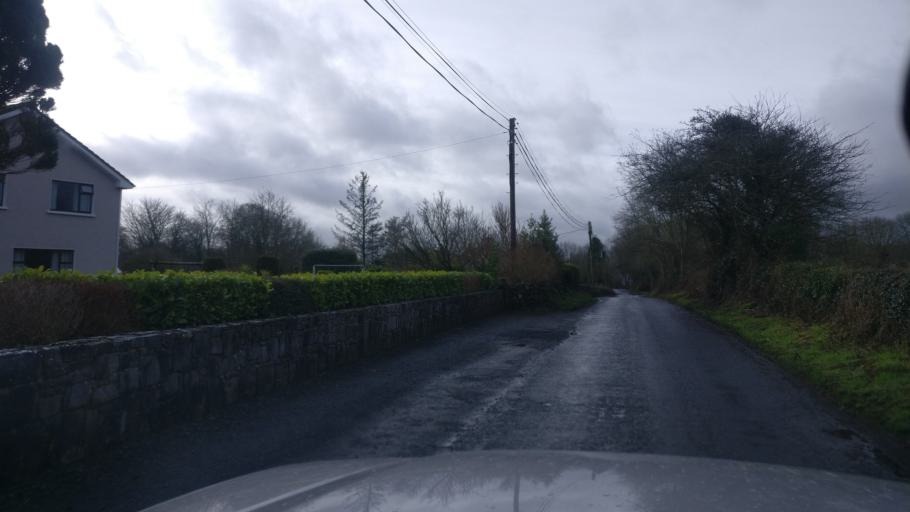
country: IE
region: Connaught
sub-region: County Galway
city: Athenry
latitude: 53.2747
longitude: -8.7679
